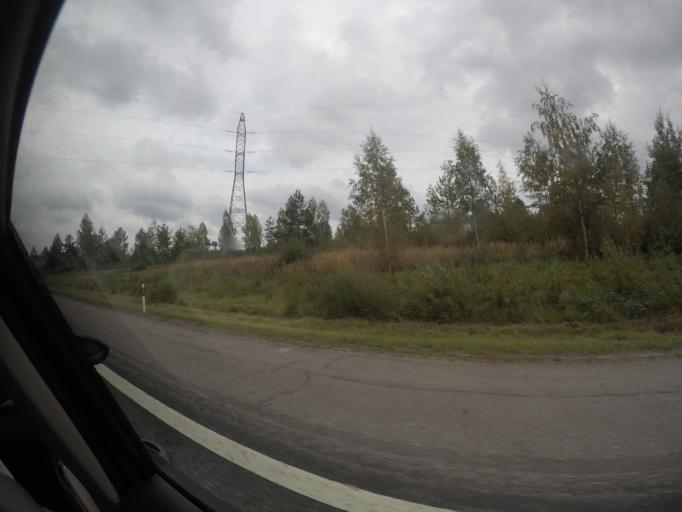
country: FI
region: Uusimaa
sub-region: Helsinki
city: Hyvinge
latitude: 60.6186
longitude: 24.8086
